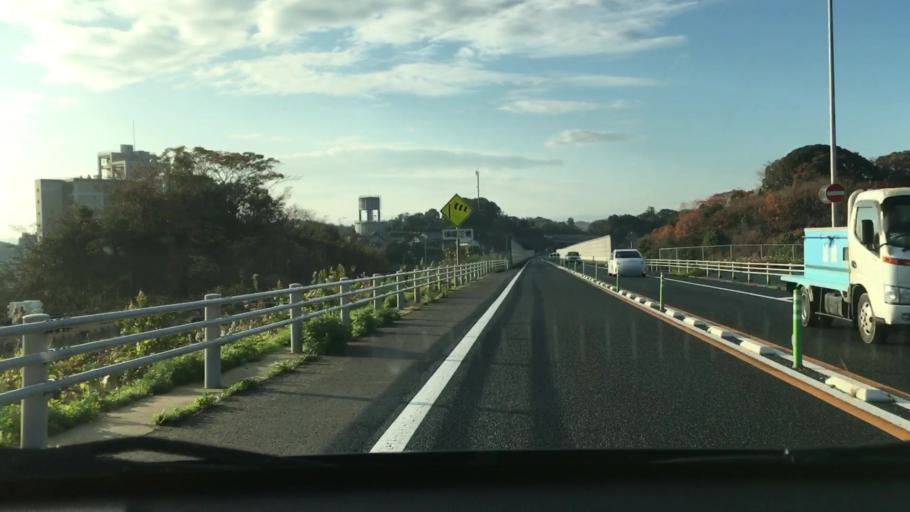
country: JP
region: Nagasaki
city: Sasebo
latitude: 33.0856
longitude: 129.7774
